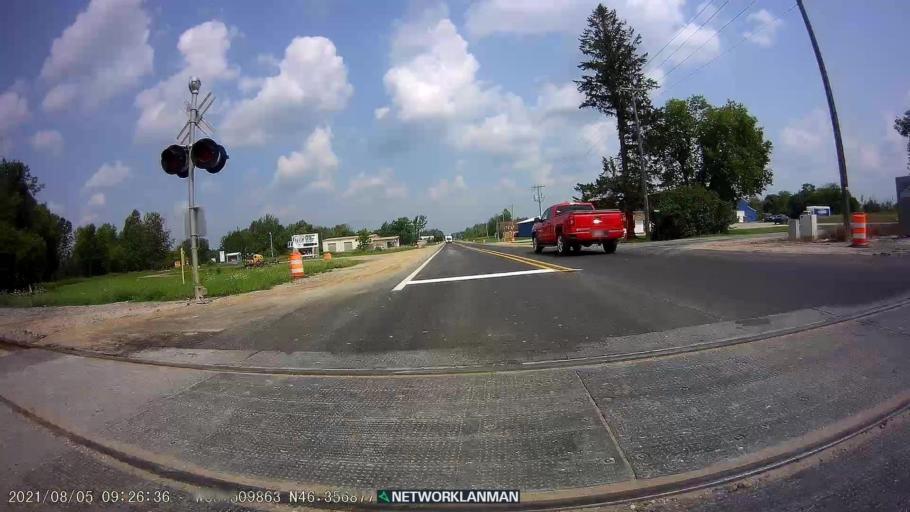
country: US
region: Michigan
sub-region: Luce County
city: Newberry
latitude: 46.3562
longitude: -85.5099
